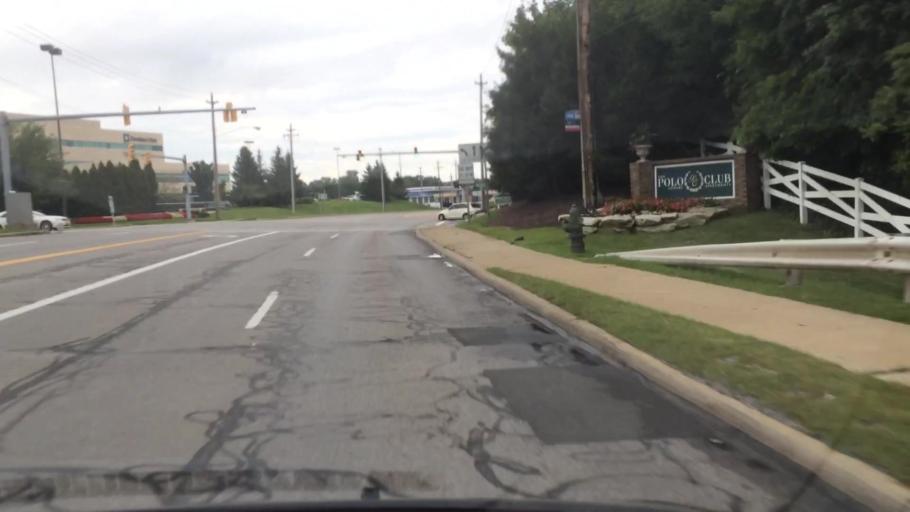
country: US
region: Ohio
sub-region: Cuyahoga County
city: Strongsville
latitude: 41.3104
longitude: -81.8155
